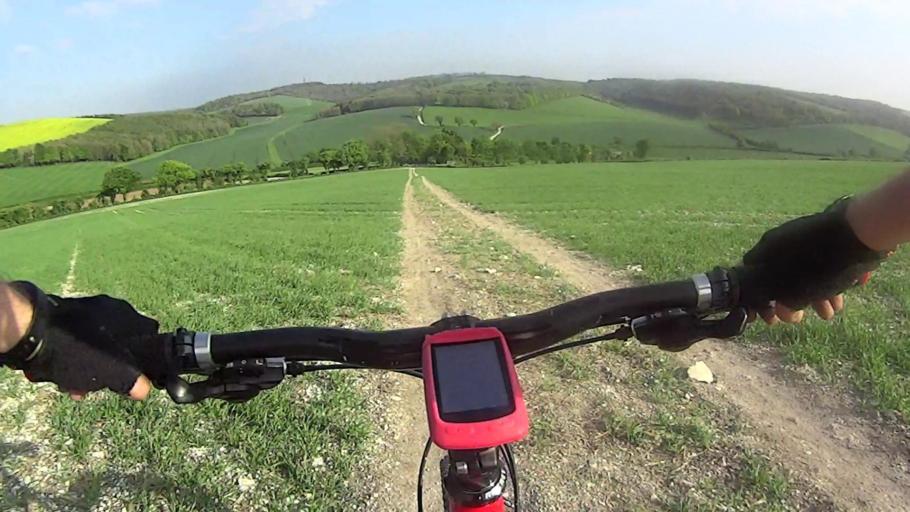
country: GB
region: England
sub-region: West Sussex
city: Fontwell
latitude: 50.9252
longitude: -0.6516
